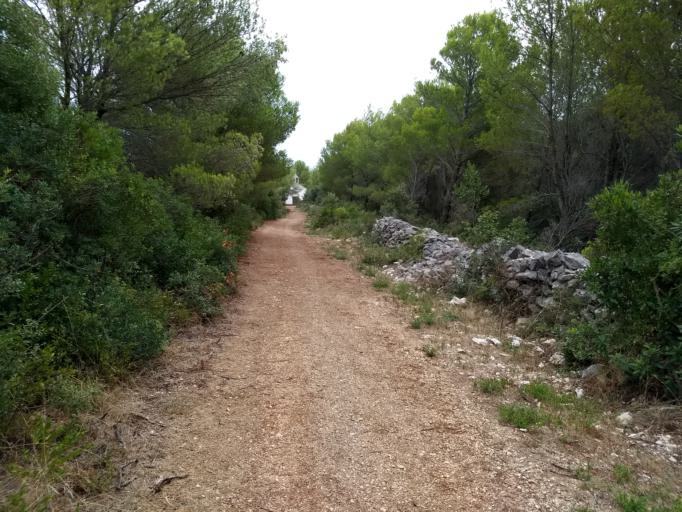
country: HR
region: Zadarska
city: Ugljan
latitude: 44.1438
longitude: 15.0787
